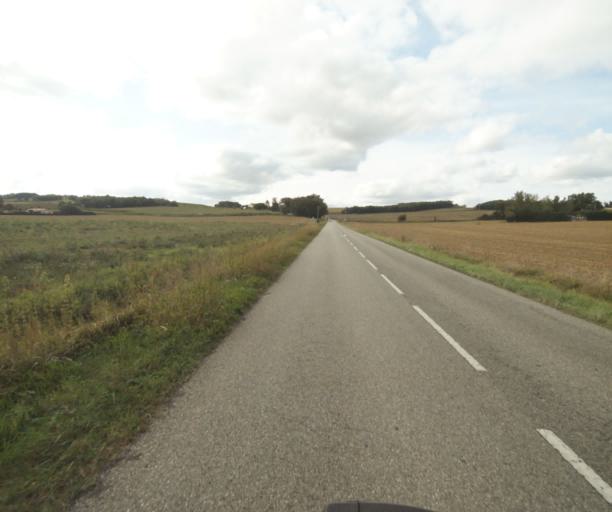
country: FR
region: Midi-Pyrenees
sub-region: Departement du Tarn-et-Garonne
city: Verdun-sur-Garonne
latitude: 43.8551
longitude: 1.1291
